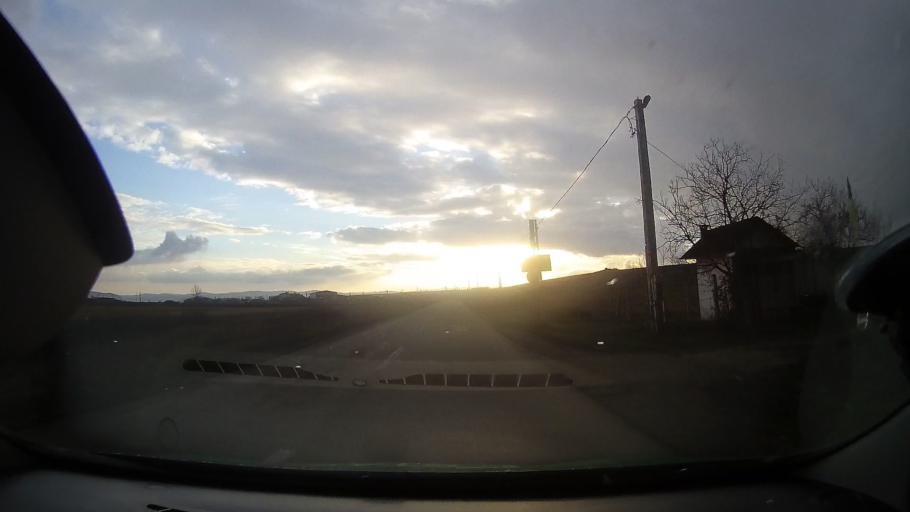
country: RO
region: Alba
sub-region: Comuna Lunca Muresului
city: Lunca Muresului
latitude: 46.4430
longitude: 23.9121
